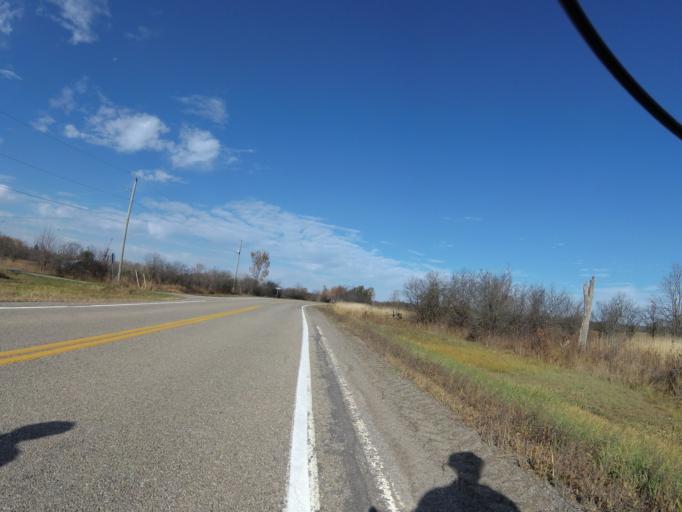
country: CA
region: Ontario
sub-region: Lanark County
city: Smiths Falls
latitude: 44.8275
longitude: -75.9396
